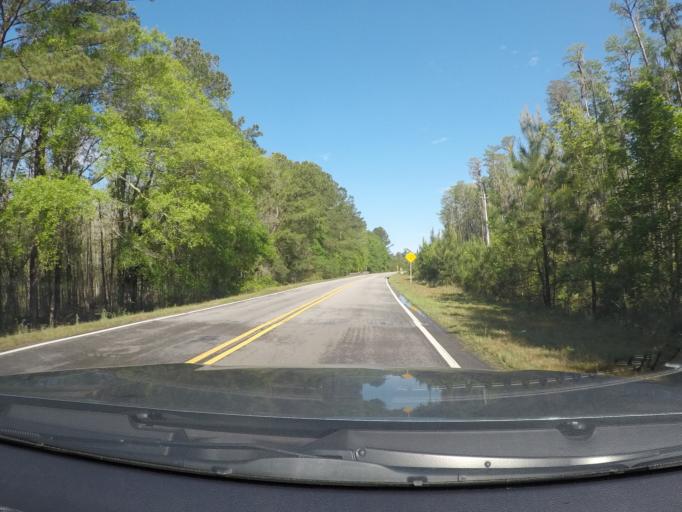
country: US
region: Georgia
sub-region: Chatham County
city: Bloomingdale
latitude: 32.0614
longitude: -81.3139
